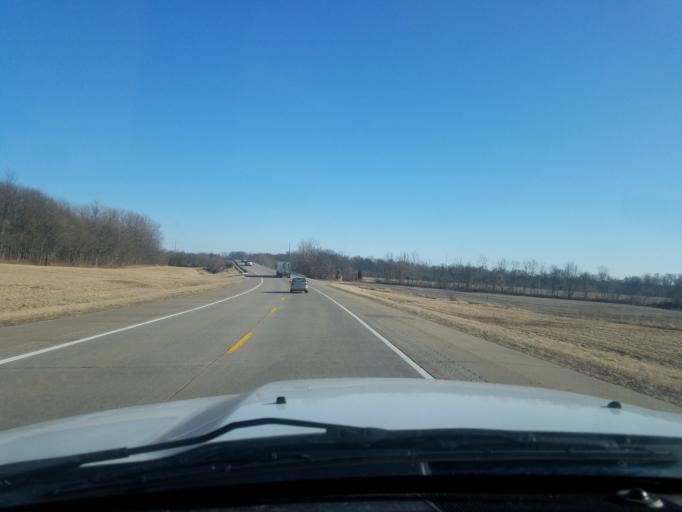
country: US
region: Kentucky
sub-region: Henderson County
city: Henderson
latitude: 37.7913
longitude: -87.6400
